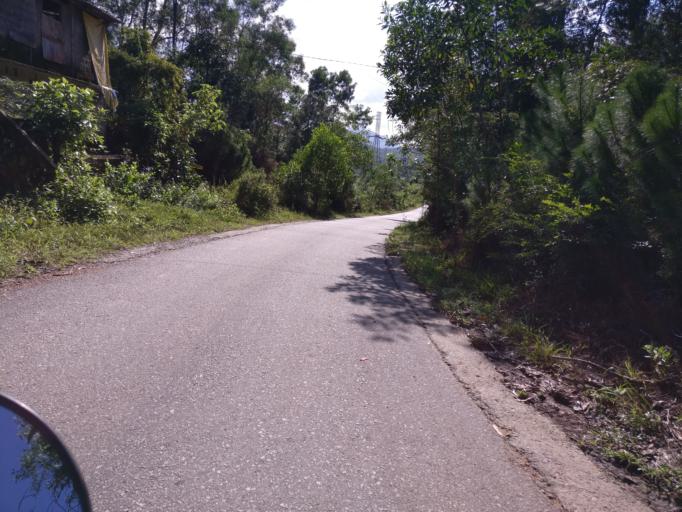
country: VN
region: Thua Thien-Hue
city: Hue
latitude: 16.4064
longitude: 107.5925
